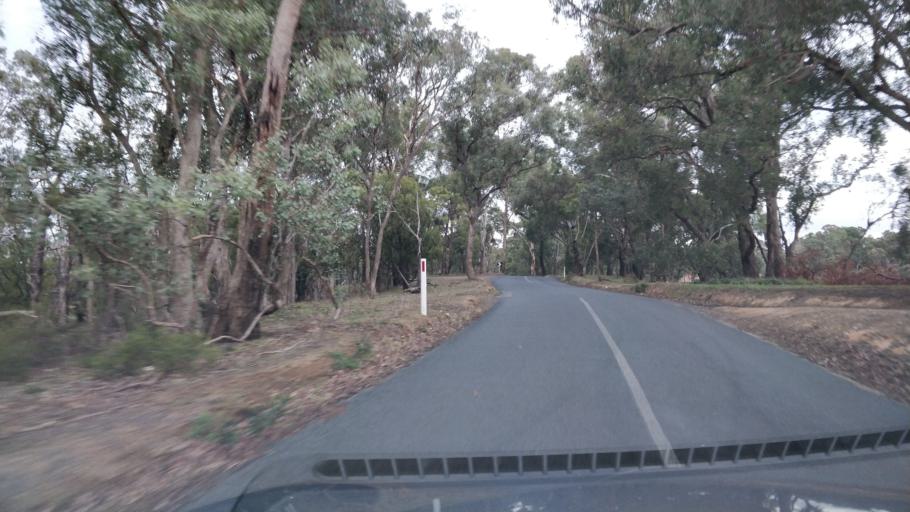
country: AU
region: Victoria
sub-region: Nillumbik
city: Research
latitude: -37.6881
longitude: 145.1783
